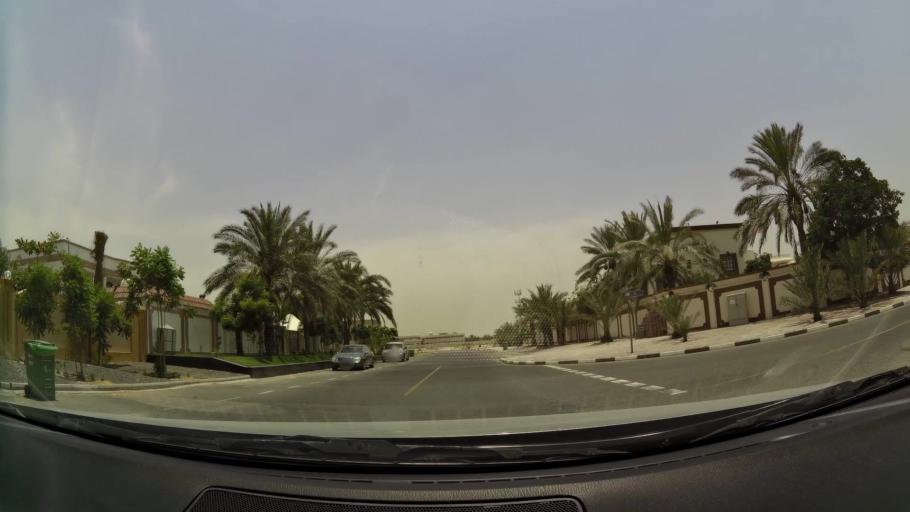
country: AE
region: Ash Shariqah
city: Sharjah
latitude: 25.2094
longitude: 55.3872
